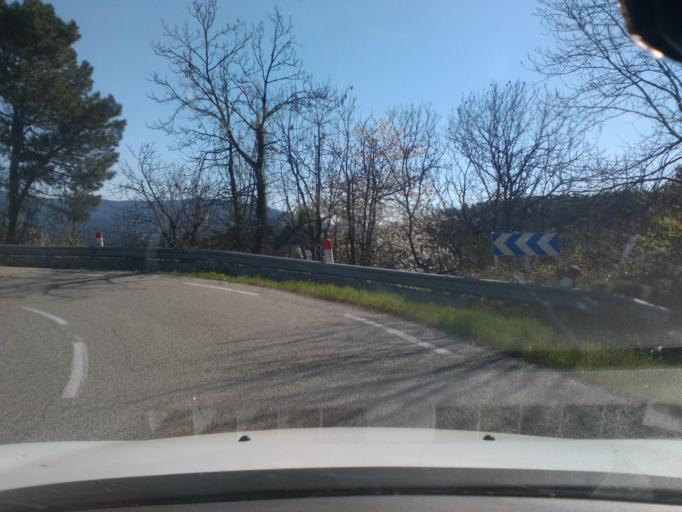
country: FR
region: Languedoc-Roussillon
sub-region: Departement du Gard
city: Saint-Jean-du-Gard
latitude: 44.1470
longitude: 3.7779
